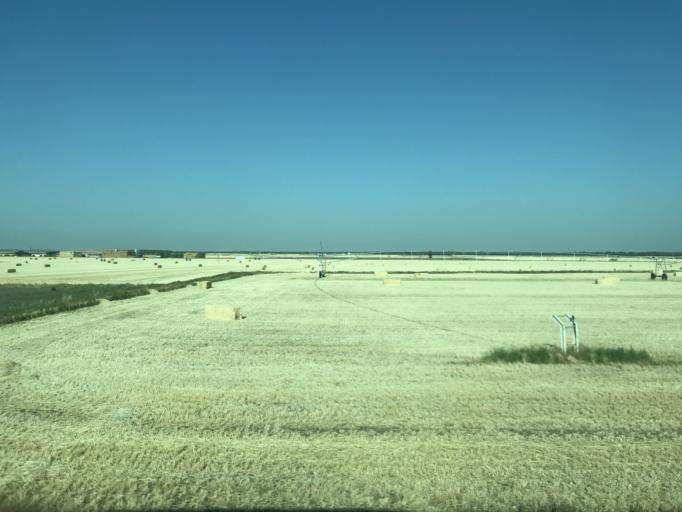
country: ES
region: Castille and Leon
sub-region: Provincia de Valladolid
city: Puras
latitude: 41.1637
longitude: -4.6545
